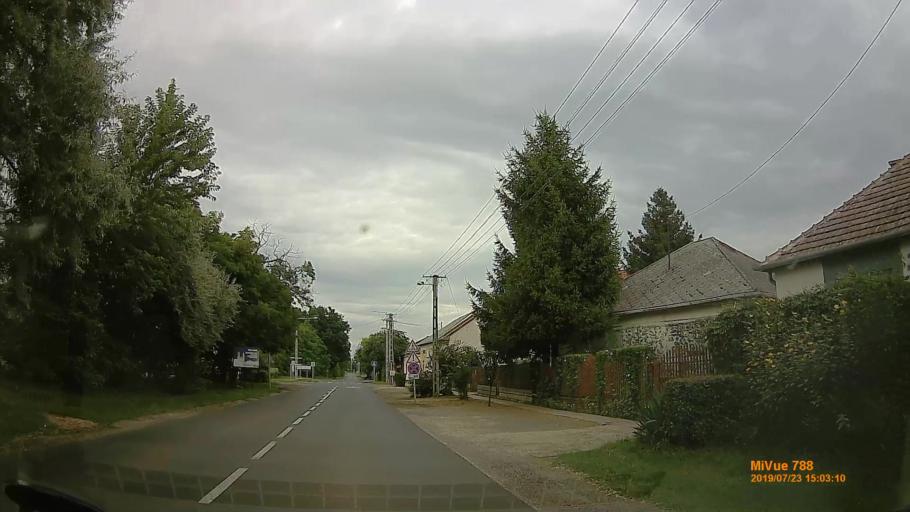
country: HU
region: Szabolcs-Szatmar-Bereg
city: Nyiregyhaza
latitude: 47.9322
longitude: 21.7085
